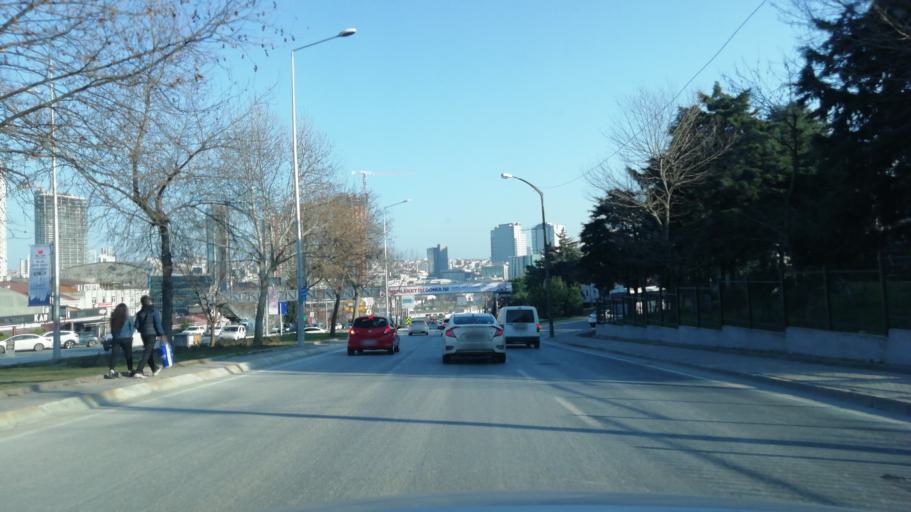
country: TR
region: Istanbul
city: Mahmutbey
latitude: 41.0467
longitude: 28.8026
